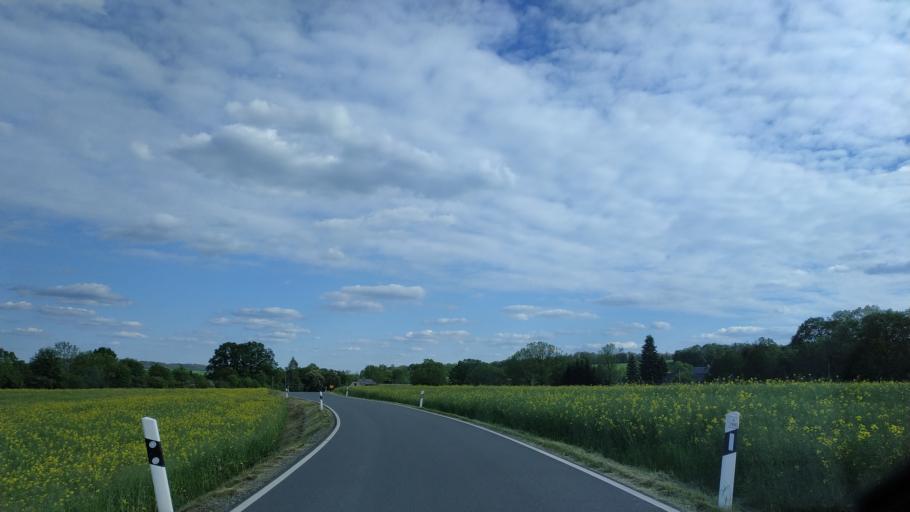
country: DE
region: Saxony
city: Pohl
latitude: 50.5502
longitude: 12.1609
